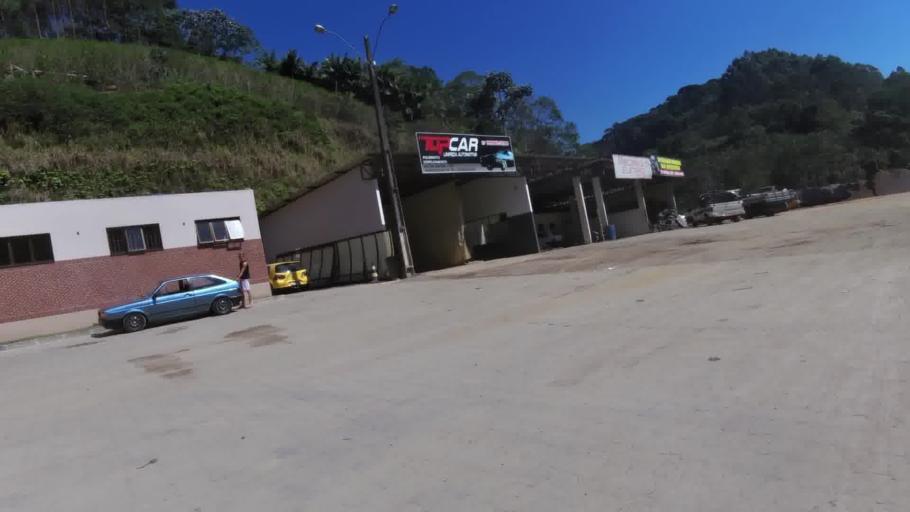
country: BR
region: Espirito Santo
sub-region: Marechal Floriano
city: Marechal Floriano
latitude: -20.4224
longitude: -40.7770
